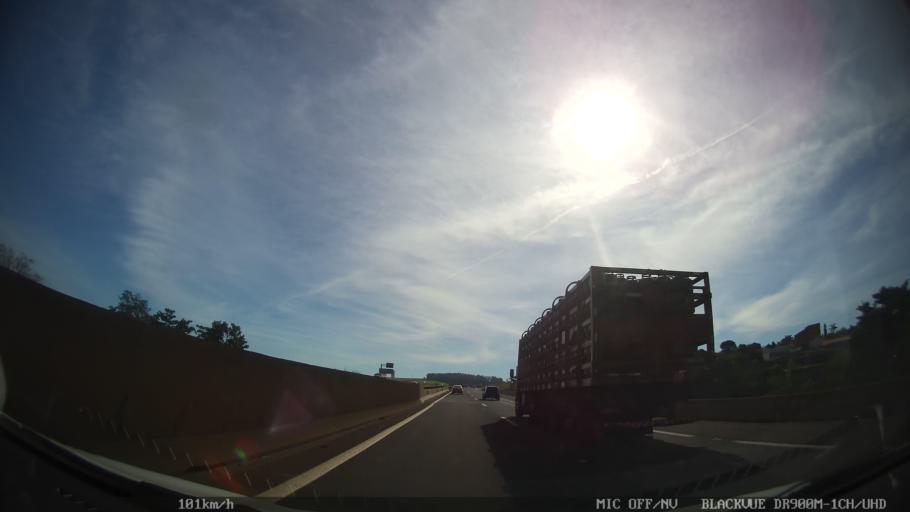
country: BR
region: Sao Paulo
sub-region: Araras
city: Araras
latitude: -22.3497
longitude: -47.3945
